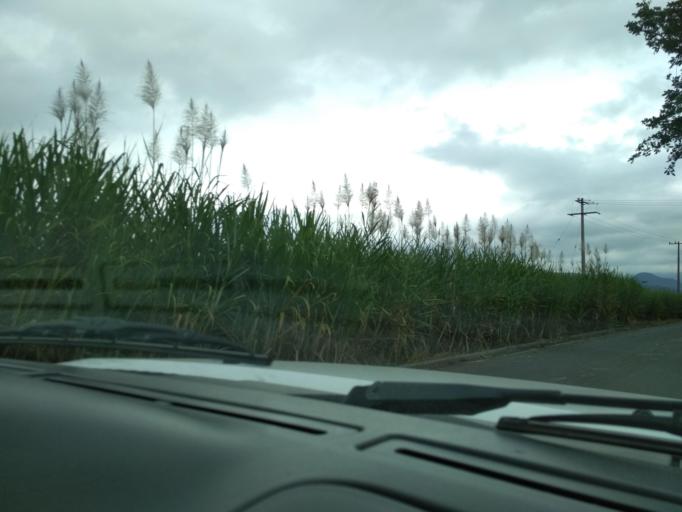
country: MX
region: Veracruz
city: El Castillo
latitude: 19.5832
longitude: -96.8235
